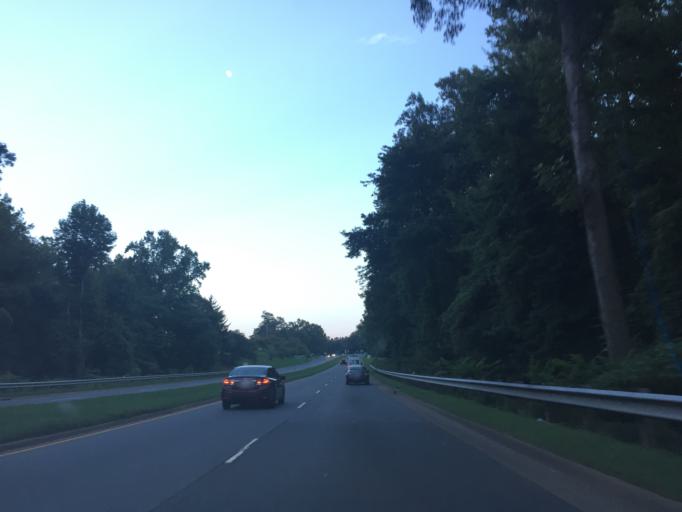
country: US
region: Virginia
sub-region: City of Charlottesville
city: Charlottesville
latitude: 38.0503
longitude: -78.4807
